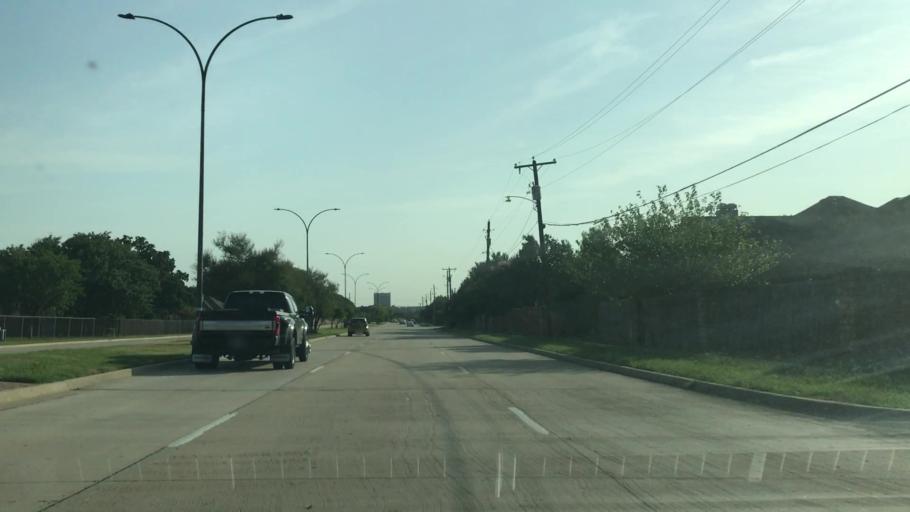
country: US
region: Texas
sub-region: Tarrant County
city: Euless
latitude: 32.7807
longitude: -97.0713
